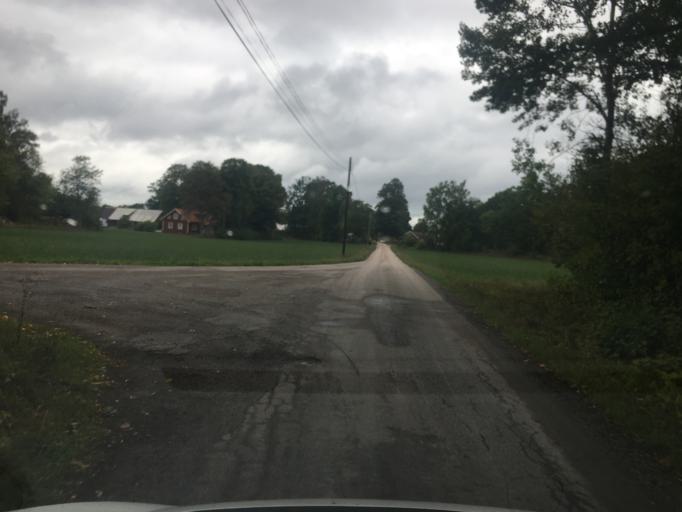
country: SE
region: Kronoberg
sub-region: Ljungby Kommun
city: Lagan
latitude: 56.9729
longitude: 14.0396
